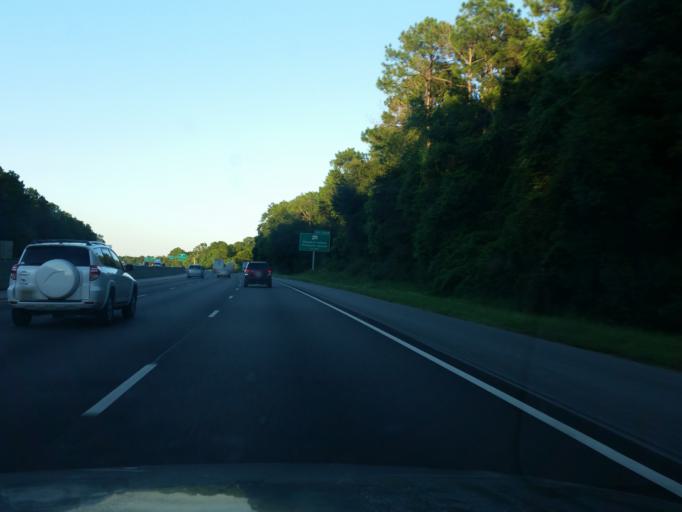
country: US
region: Alabama
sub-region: Mobile County
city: Tillmans Corner
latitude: 30.5862
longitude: -88.1614
